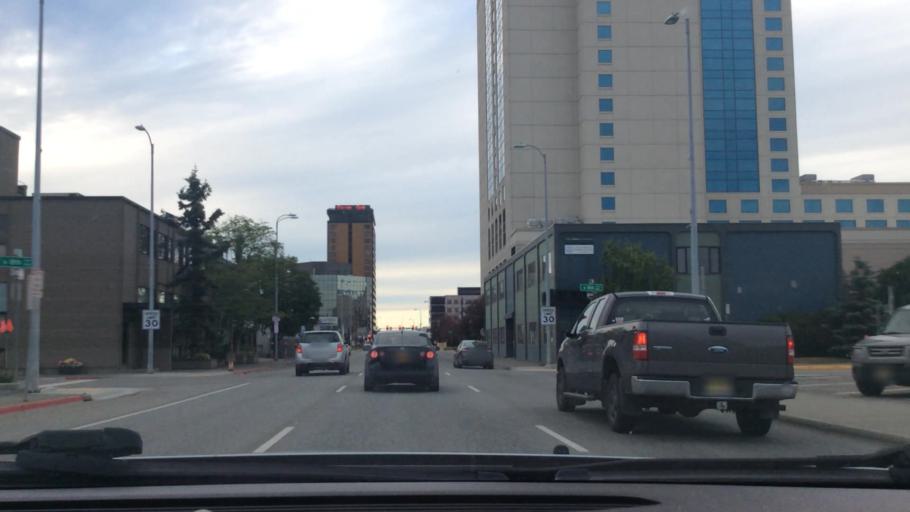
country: US
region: Alaska
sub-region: Anchorage Municipality
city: Anchorage
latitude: 61.2144
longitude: -149.8995
